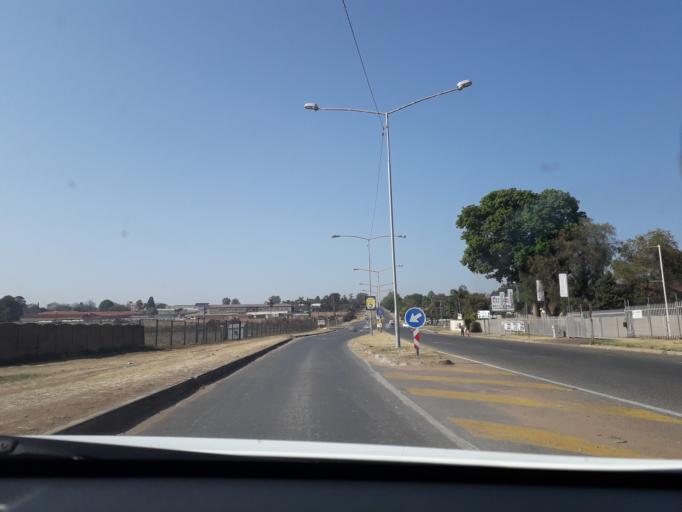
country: ZA
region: Gauteng
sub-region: City of Johannesburg Metropolitan Municipality
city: Modderfontein
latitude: -26.0856
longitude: 28.2493
